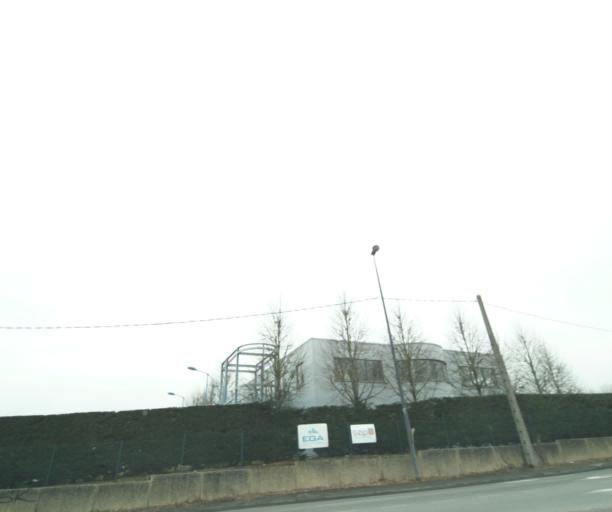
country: FR
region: Ile-de-France
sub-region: Departement de l'Essonne
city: Saulx-les-Chartreux
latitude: 48.6990
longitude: 2.2688
